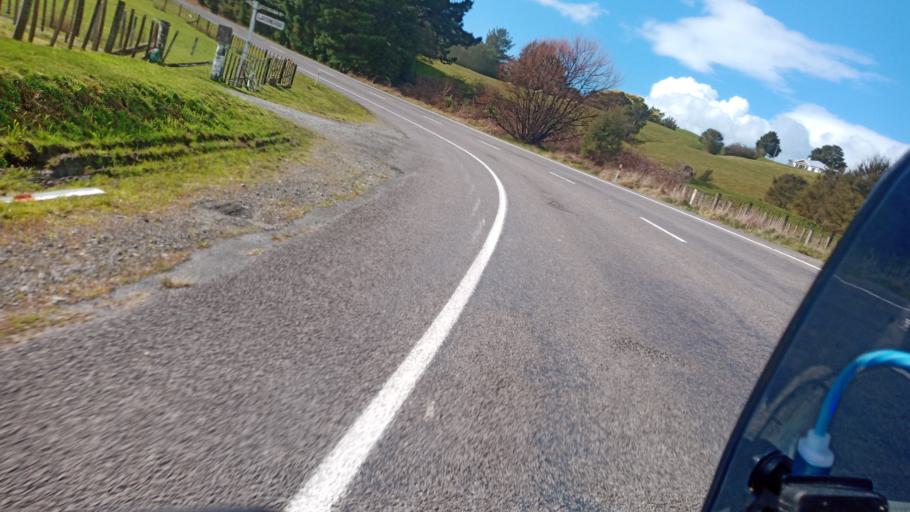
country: NZ
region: Gisborne
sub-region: Gisborne District
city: Gisborne
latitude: -37.9044
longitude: 178.2768
